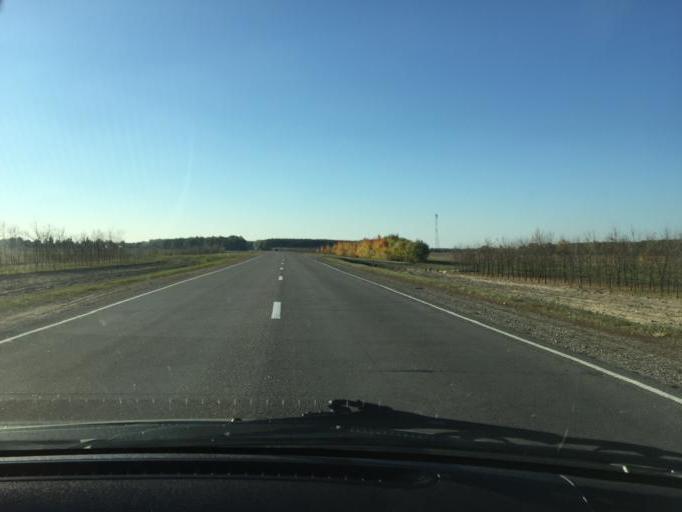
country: BY
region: Brest
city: Luninyets
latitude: 52.2748
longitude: 26.9767
